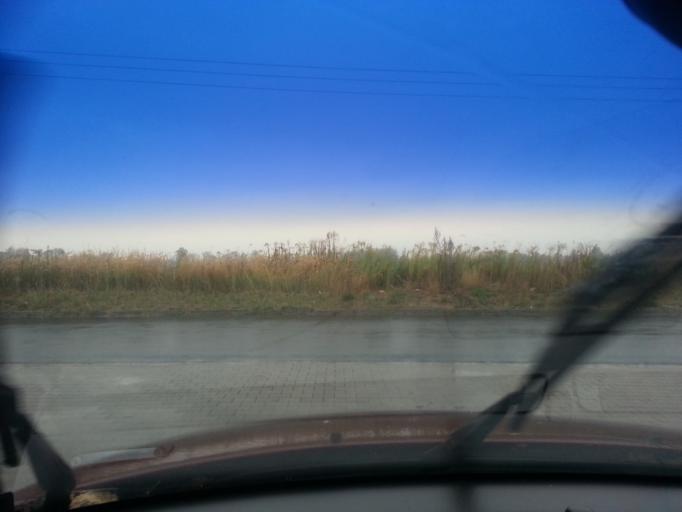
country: PL
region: Lower Silesian Voivodeship
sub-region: Powiat zgorzelecki
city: Lagow
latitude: 51.1584
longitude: 15.0352
